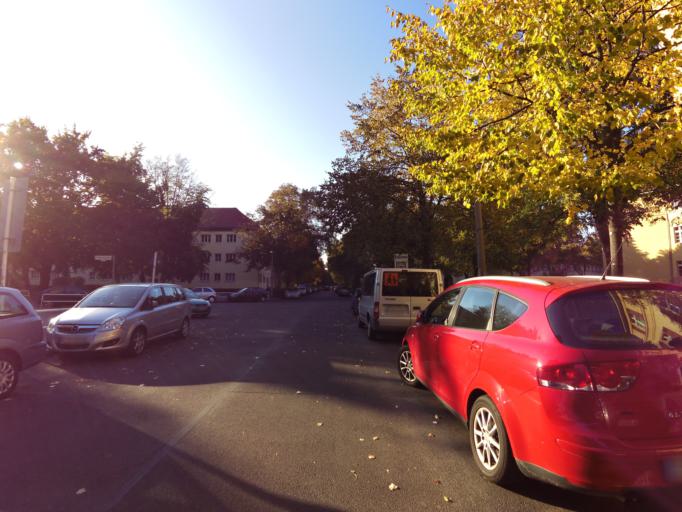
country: DE
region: Berlin
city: Oberschoneweide
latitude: 52.4661
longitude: 13.5183
